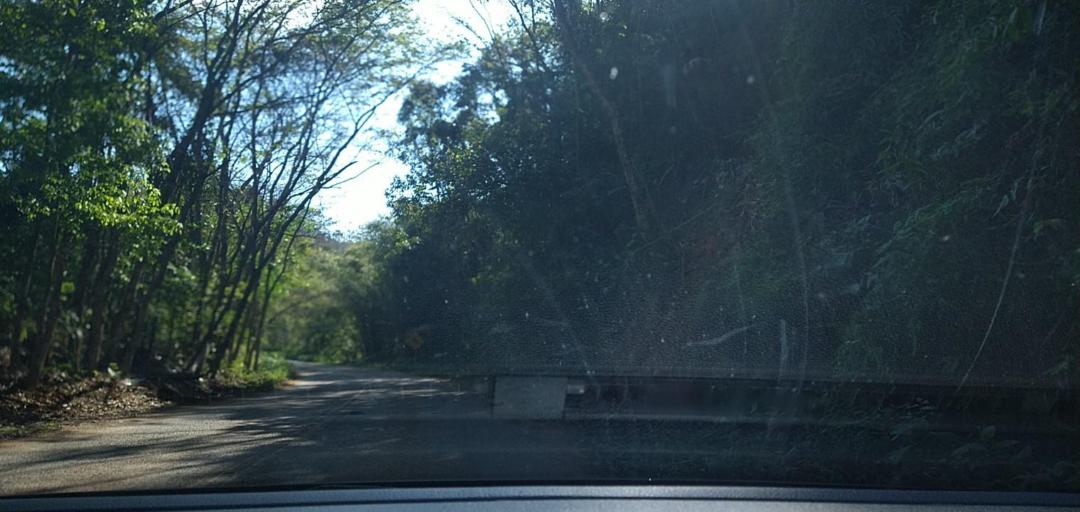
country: BR
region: Minas Gerais
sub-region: Alvinopolis
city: Alvinopolis
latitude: -20.1764
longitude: -42.9291
